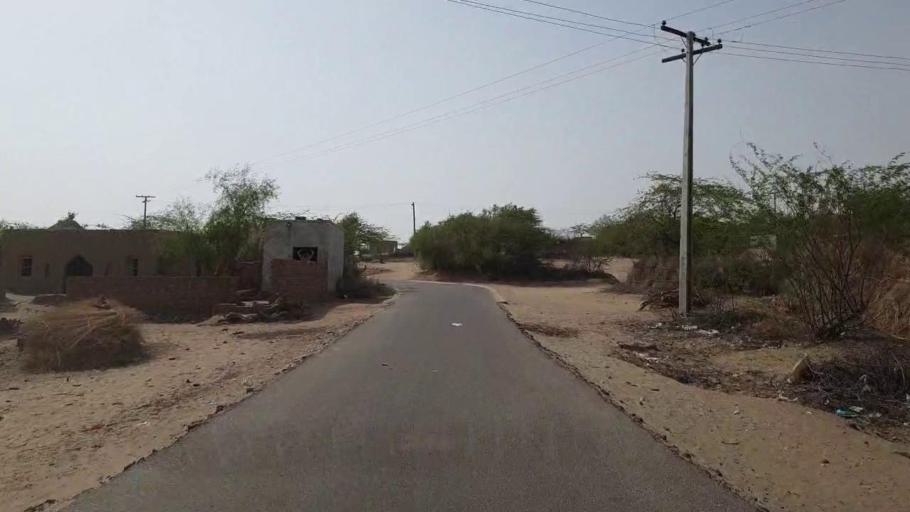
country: PK
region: Sindh
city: Mithi
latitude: 24.5758
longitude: 69.9286
